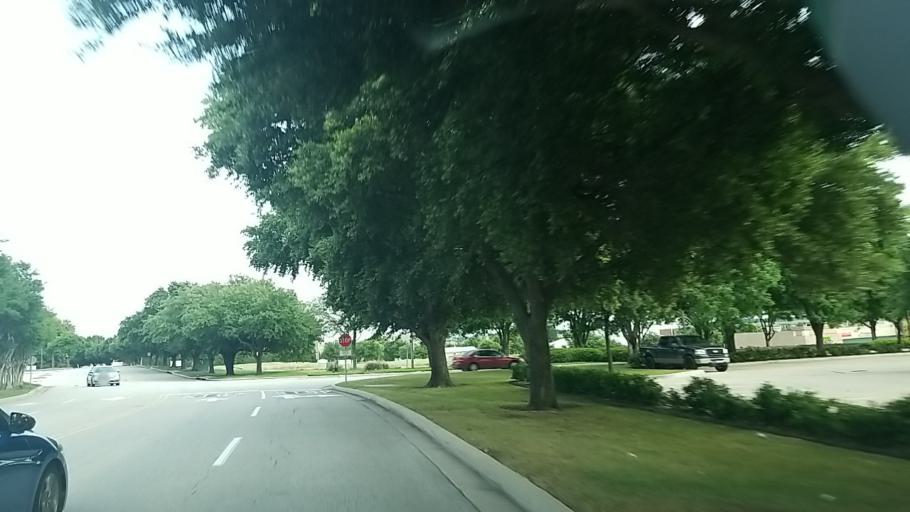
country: US
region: Texas
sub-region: Denton County
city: Lewisville
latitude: 33.0021
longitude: -96.9756
